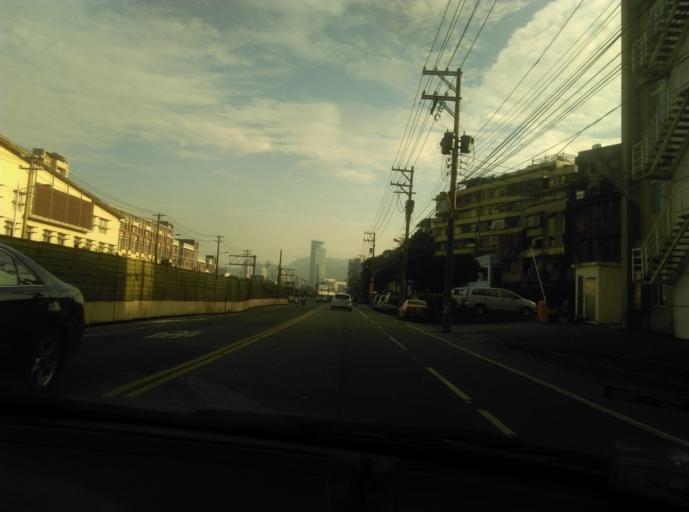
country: TW
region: Taiwan
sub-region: Keelung
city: Keelung
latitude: 25.1429
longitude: 121.7381
